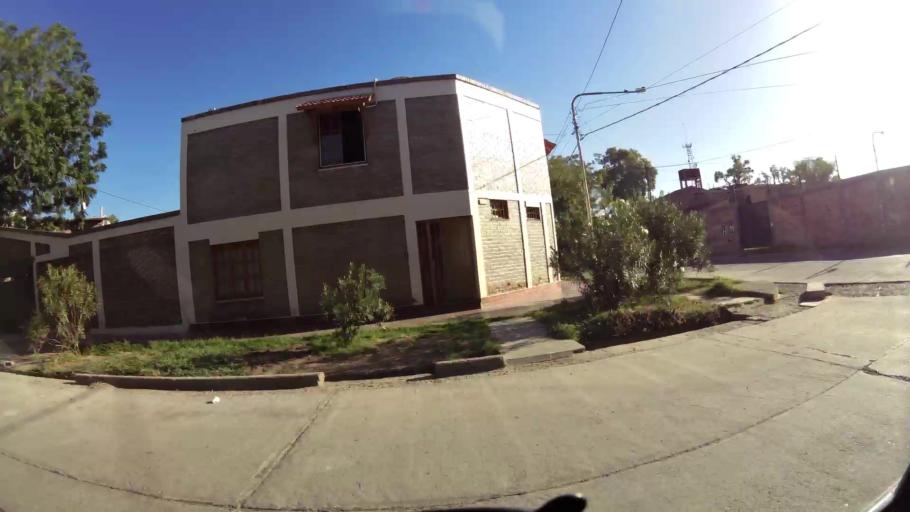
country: AR
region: Mendoza
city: Las Heras
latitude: -32.8587
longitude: -68.8289
